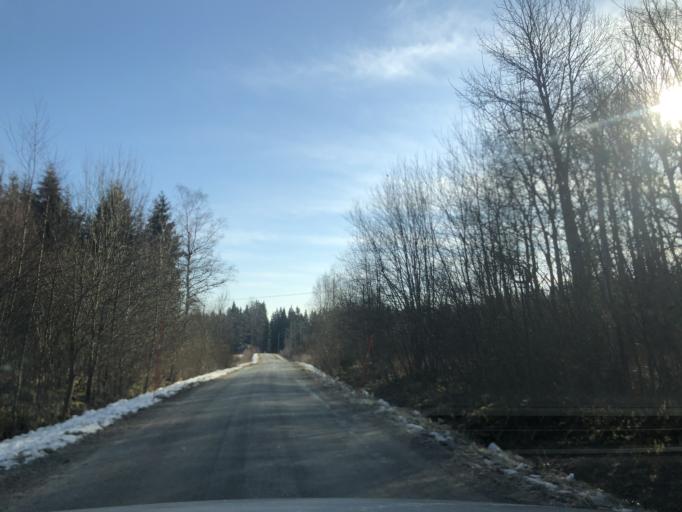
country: SE
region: Vaestra Goetaland
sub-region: Ulricehamns Kommun
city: Ulricehamn
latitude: 57.7958
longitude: 13.4507
